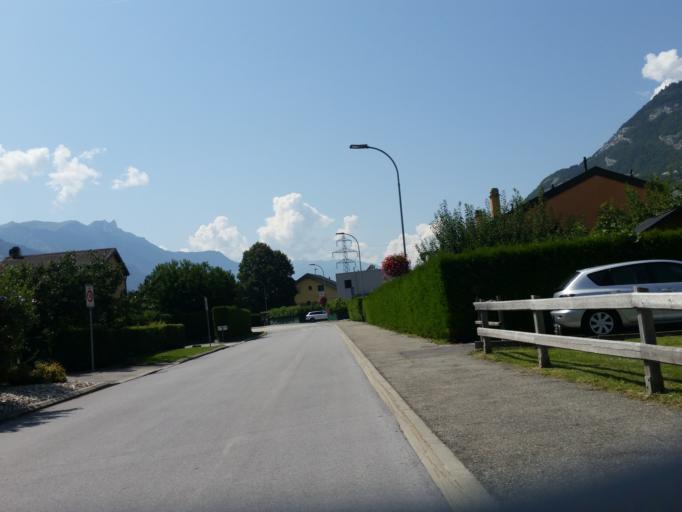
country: CH
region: Valais
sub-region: Conthey District
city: Vetroz
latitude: 46.2216
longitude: 7.2743
